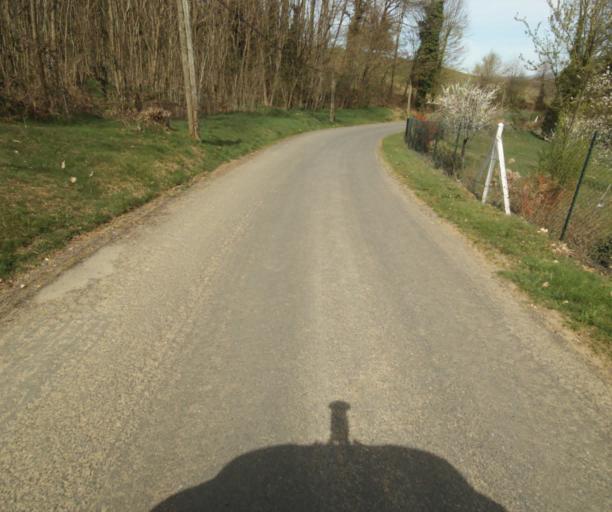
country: FR
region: Limousin
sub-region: Departement de la Correze
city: Naves
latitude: 45.3339
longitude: 1.7672
